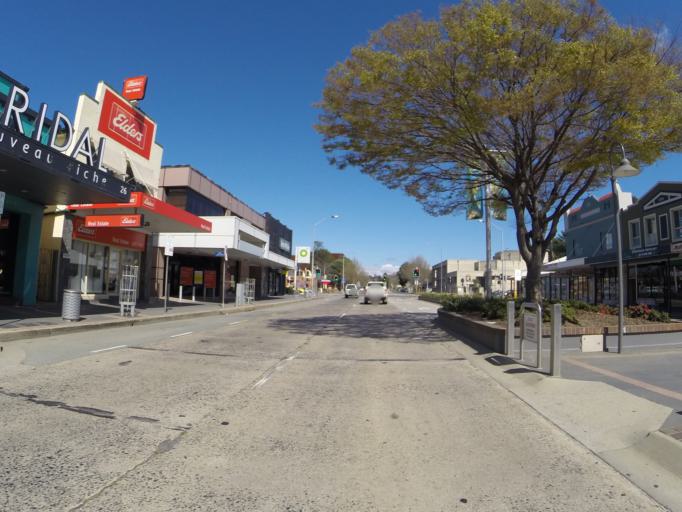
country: AU
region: New South Wales
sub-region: Queanbeyan
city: Queanbeyan
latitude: -35.3540
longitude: 149.2332
